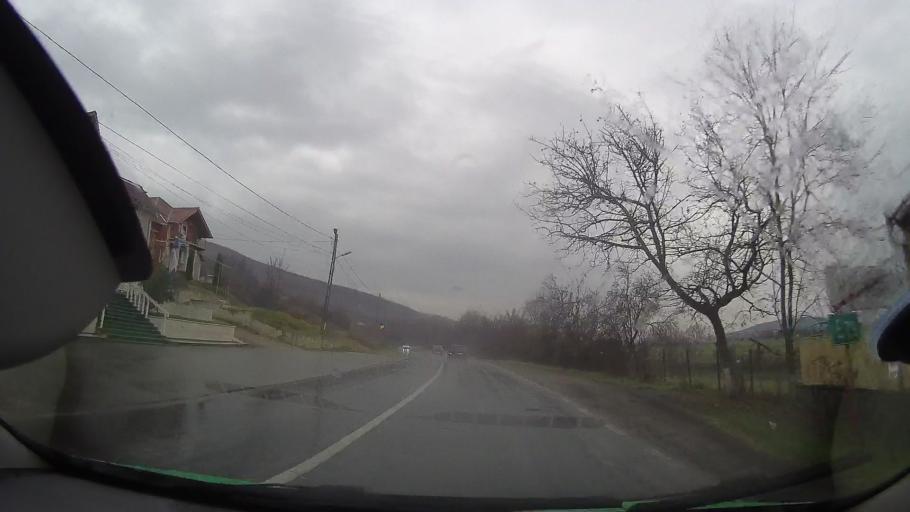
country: RO
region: Bihor
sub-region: Comuna Rabagani
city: Rabagani
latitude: 46.7514
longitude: 22.2123
